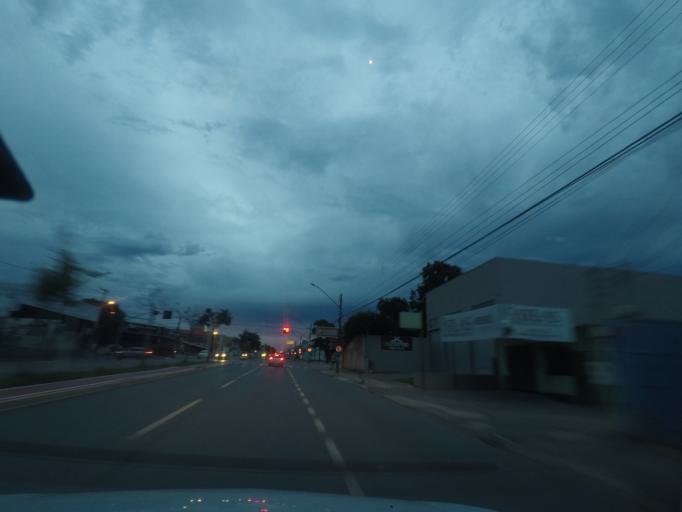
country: BR
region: Goias
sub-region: Goiania
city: Goiania
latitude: -16.7185
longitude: -49.2965
